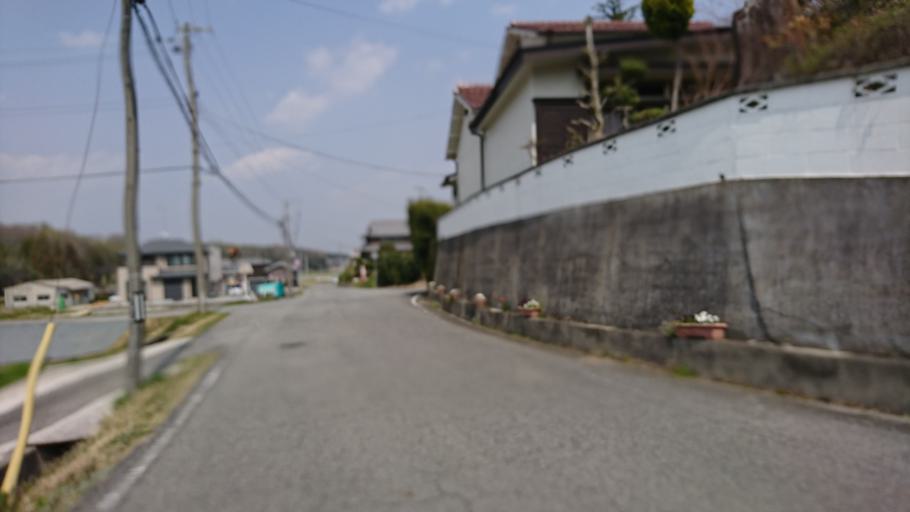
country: JP
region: Hyogo
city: Ono
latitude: 34.8315
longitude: 134.9038
